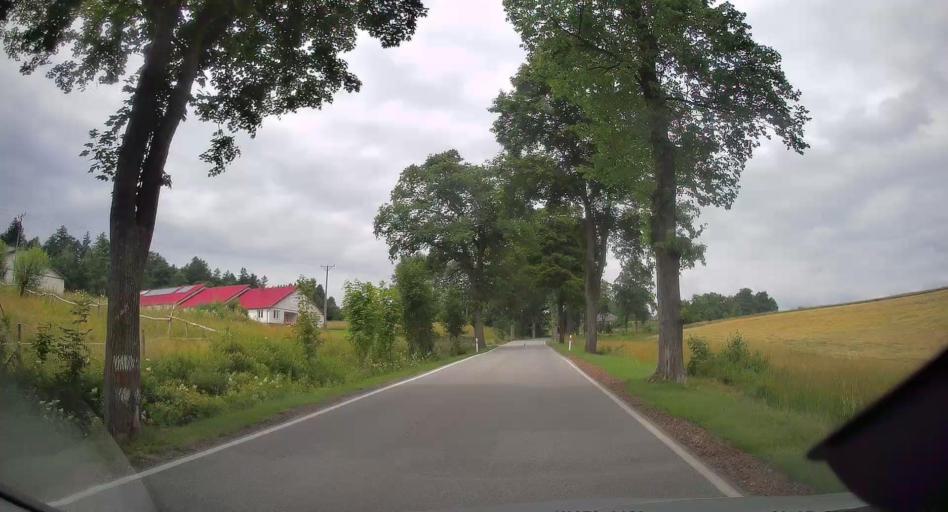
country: PL
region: Lower Silesian Voivodeship
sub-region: Powiat walbrzyski
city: Jedlina-Zdroj
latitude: 50.7342
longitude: 16.3506
